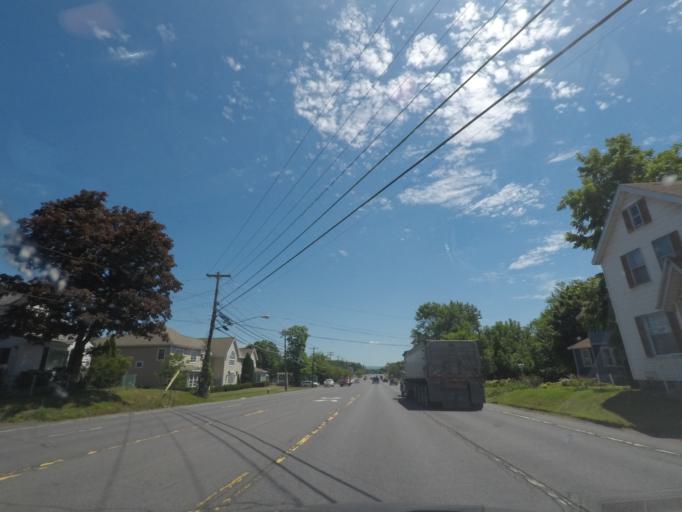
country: US
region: New York
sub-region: Albany County
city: Watervliet
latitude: 42.7458
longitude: -73.7553
